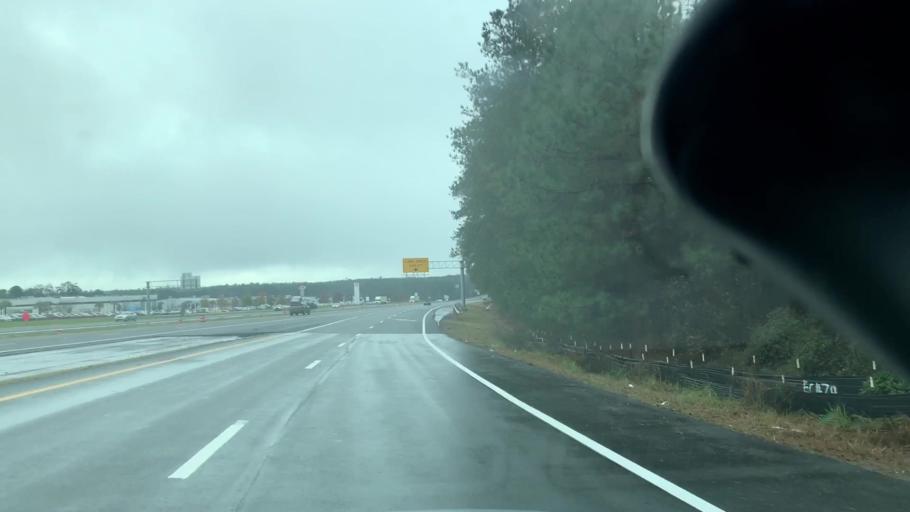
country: US
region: South Carolina
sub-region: Richland County
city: Dentsville
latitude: 34.1324
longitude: -80.9635
